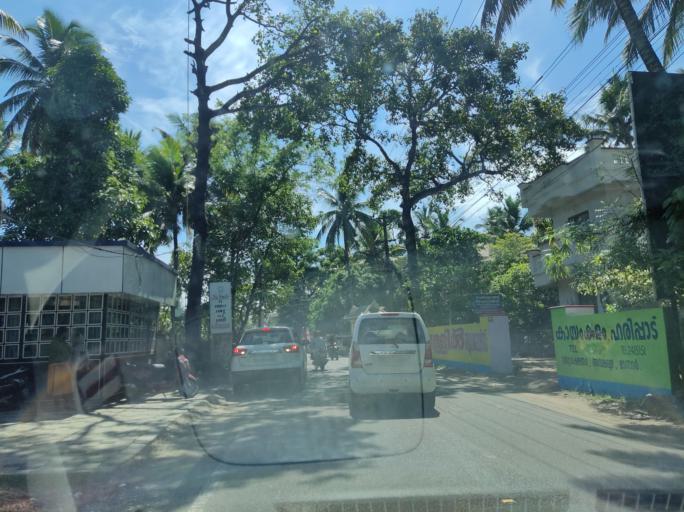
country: IN
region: Kerala
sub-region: Alappuzha
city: Kayankulam
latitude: 9.1776
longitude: 76.4899
